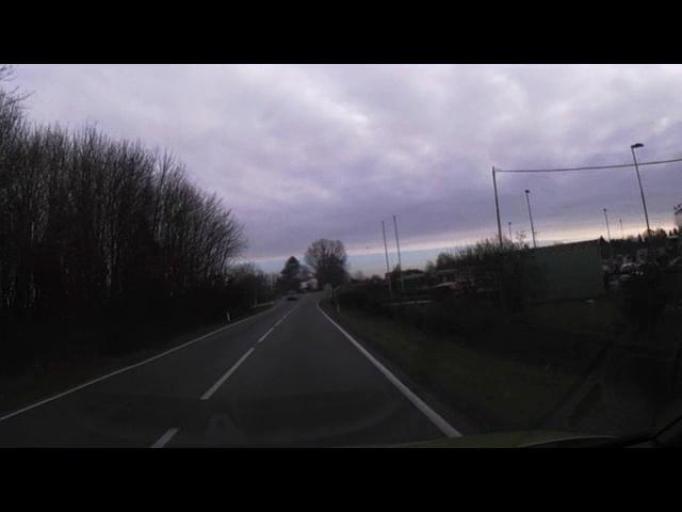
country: AT
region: Lower Austria
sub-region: Politischer Bezirk Wiener Neustadt
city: Ebenfurth
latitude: 47.8810
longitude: 16.3608
